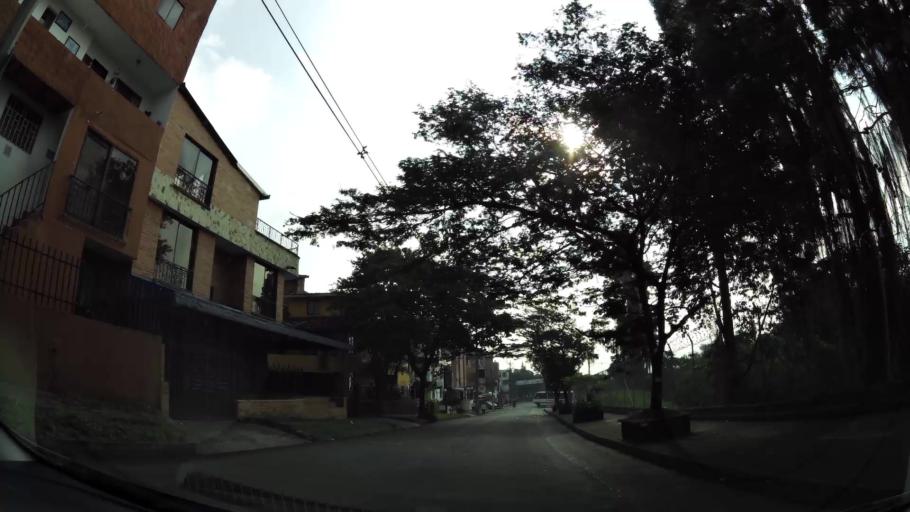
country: CO
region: Antioquia
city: Sabaneta
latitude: 6.1642
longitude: -75.6275
